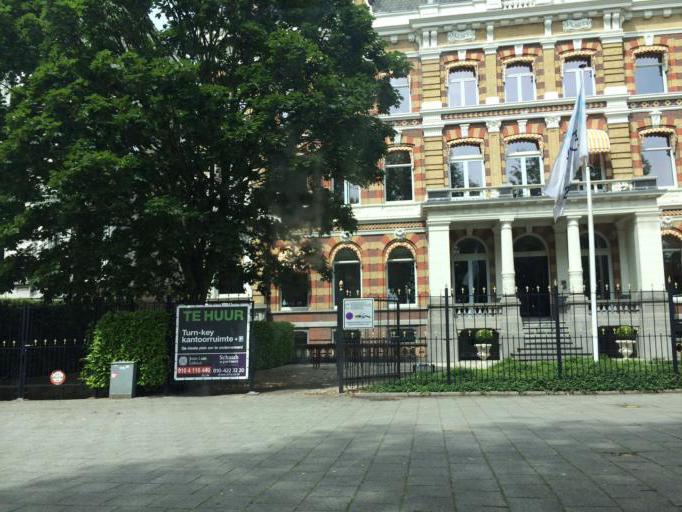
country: NL
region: South Holland
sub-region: Gemeente Rotterdam
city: Rotterdam
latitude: 51.9085
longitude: 4.4776
